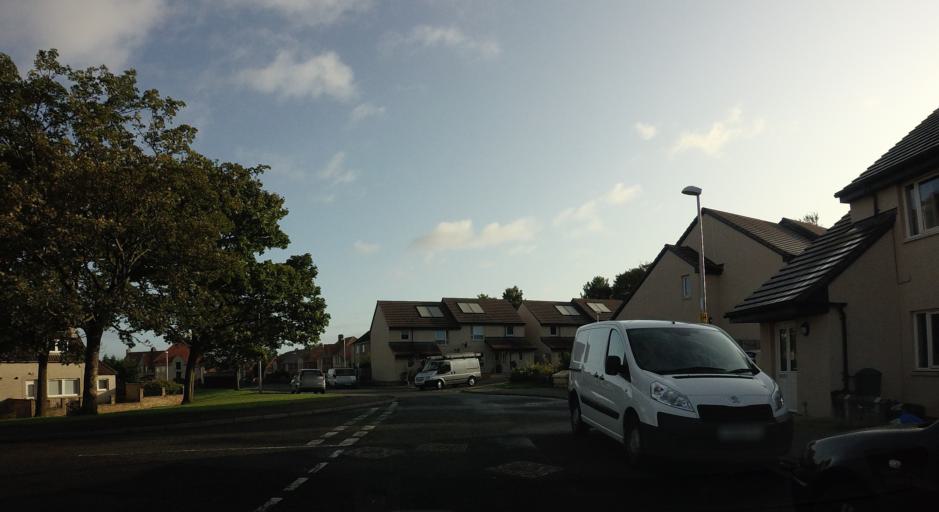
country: GB
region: Scotland
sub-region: East Lothian
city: Musselburgh
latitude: 55.9164
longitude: -3.0342
